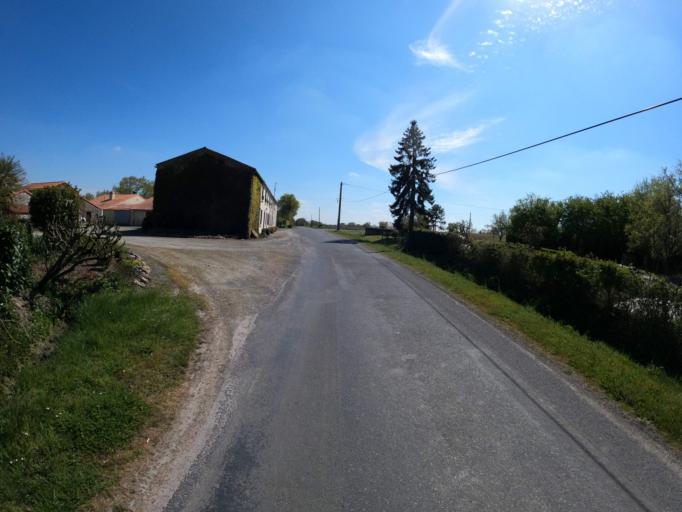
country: FR
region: Pays de la Loire
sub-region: Departement de la Loire-Atlantique
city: Remouille
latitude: 47.0304
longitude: -1.3837
